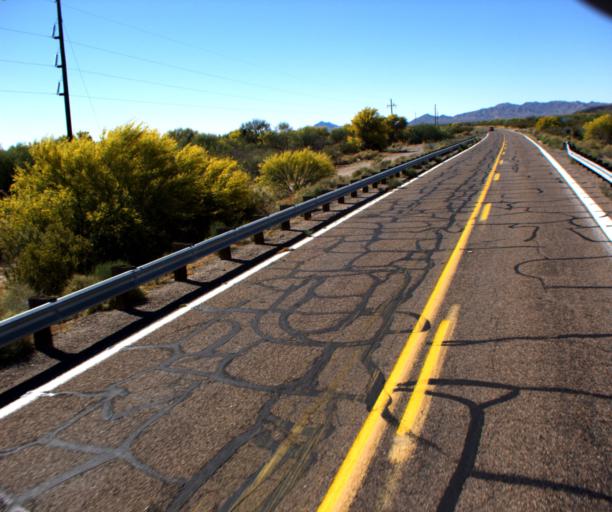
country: US
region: Arizona
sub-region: Pima County
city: Ajo
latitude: 32.4986
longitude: -112.8815
